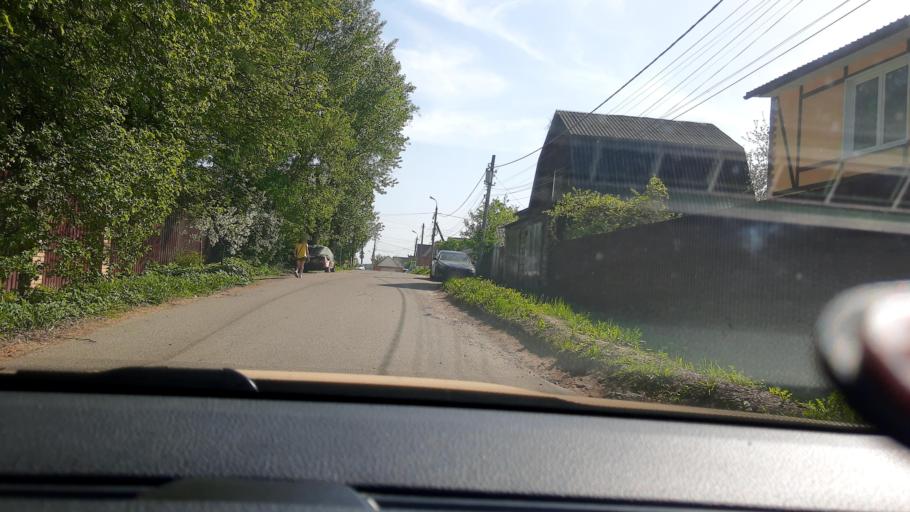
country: RU
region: Moskovskaya
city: Skhodnya
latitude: 55.9441
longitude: 37.3081
